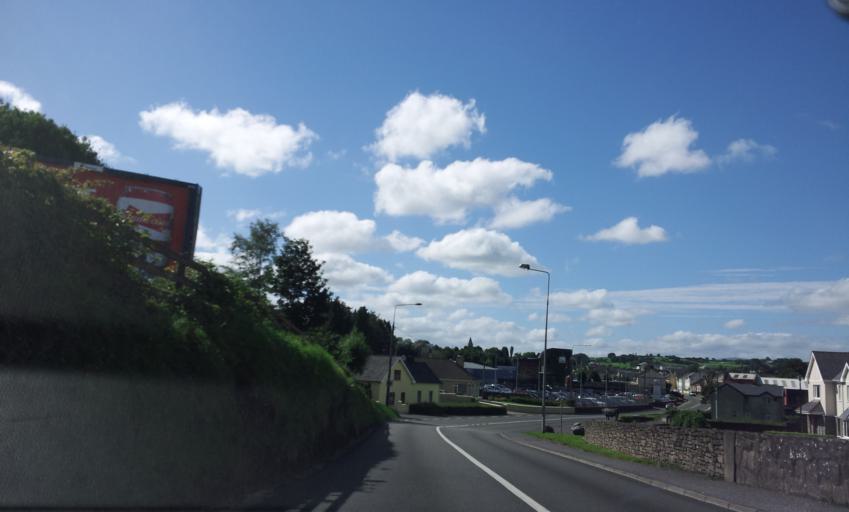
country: IE
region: Munster
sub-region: County Cork
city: Macroom
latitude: 51.9020
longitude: -8.9436
